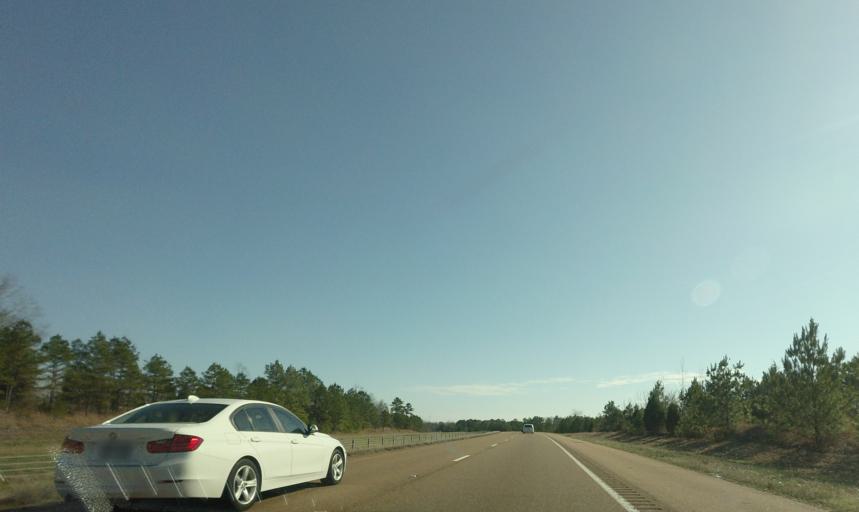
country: US
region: Mississippi
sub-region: Union County
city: New Albany
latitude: 34.5256
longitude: -89.0784
